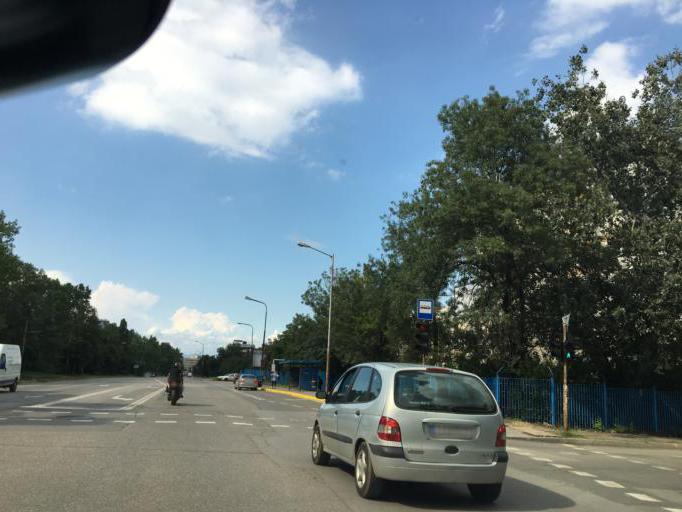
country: BG
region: Sofia-Capital
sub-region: Stolichna Obshtina
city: Sofia
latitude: 42.6572
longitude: 23.3591
